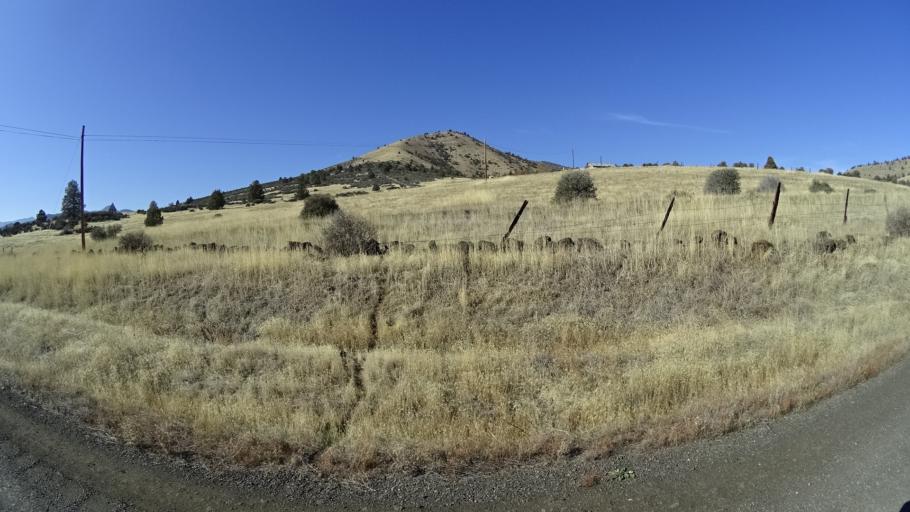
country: US
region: California
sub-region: Siskiyou County
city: Yreka
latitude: 41.7783
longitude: -122.5966
